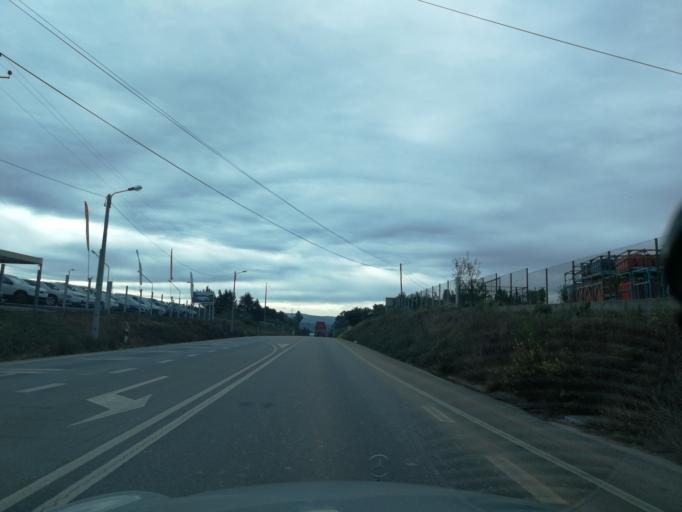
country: PT
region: Aveiro
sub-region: Albergaria-A-Velha
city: Albergaria-a-Velha
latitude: 40.6580
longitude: -8.4718
